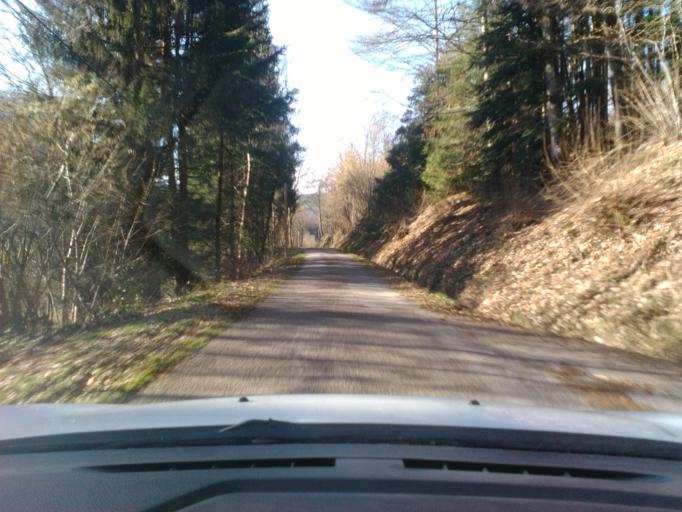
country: FR
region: Lorraine
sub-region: Departement des Vosges
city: Vecoux
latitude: 47.9740
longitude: 6.6593
